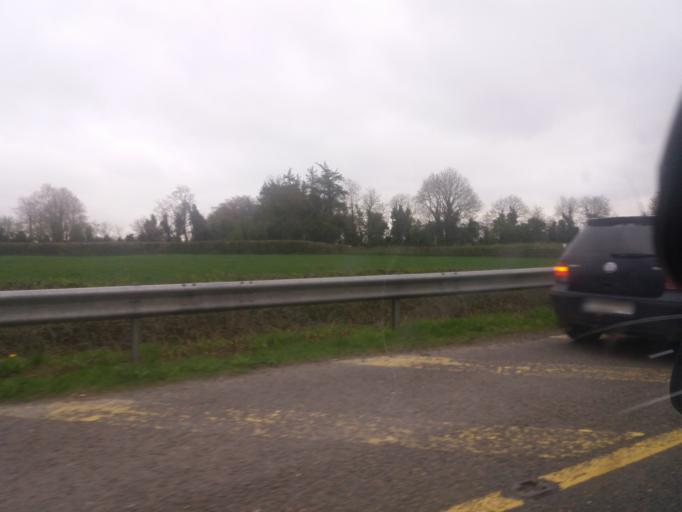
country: IE
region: Munster
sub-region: County Limerick
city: Adare
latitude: 52.5763
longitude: -8.7645
